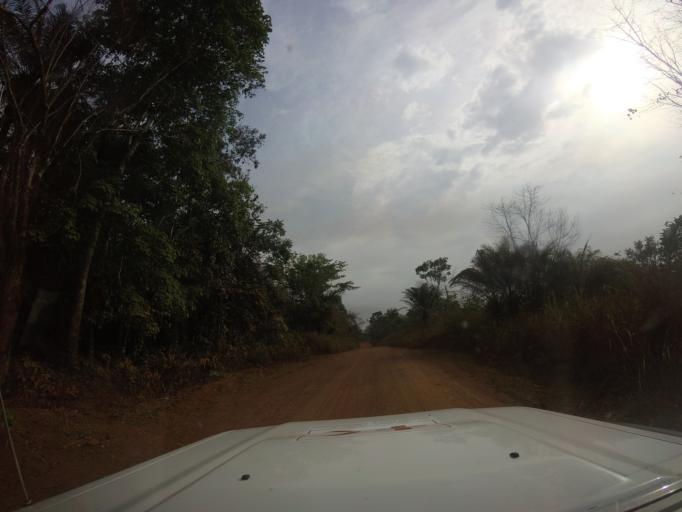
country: LR
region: Grand Cape Mount
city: Robertsport
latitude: 6.9832
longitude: -11.3033
